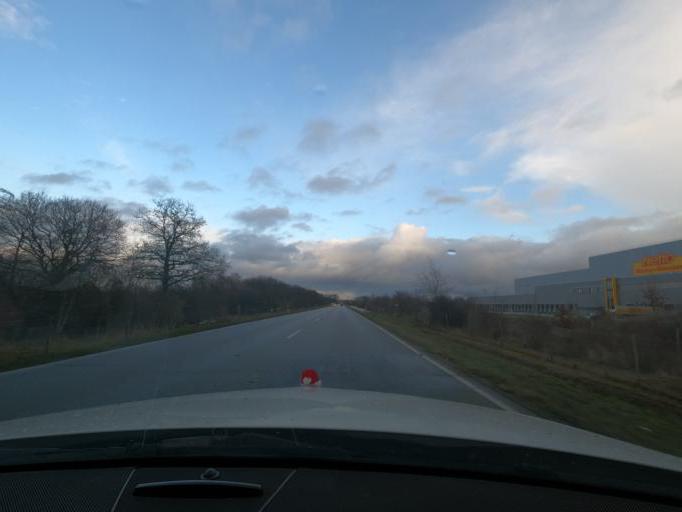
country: DE
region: Schleswig-Holstein
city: Kaltenkirchen
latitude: 53.8082
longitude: 9.9489
